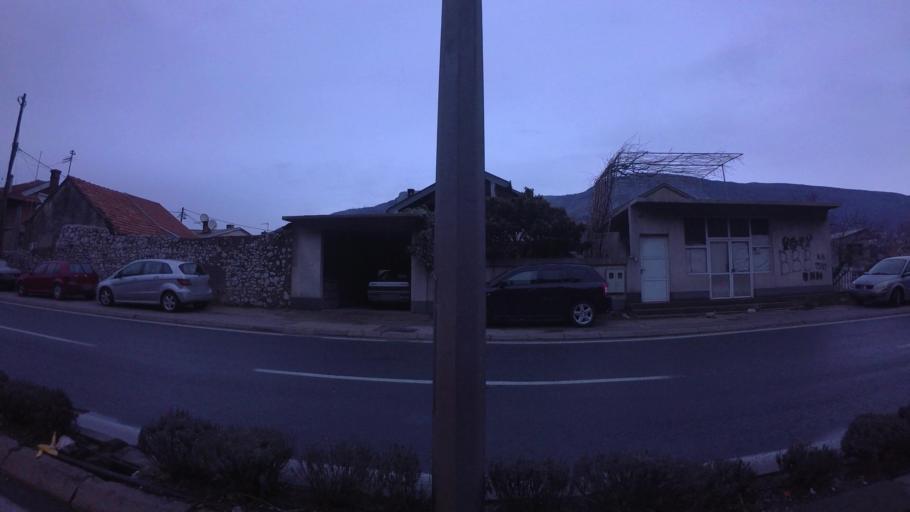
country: BA
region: Federation of Bosnia and Herzegovina
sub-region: Hercegovacko-Bosanski Kanton
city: Mostar
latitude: 43.3349
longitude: 17.8132
